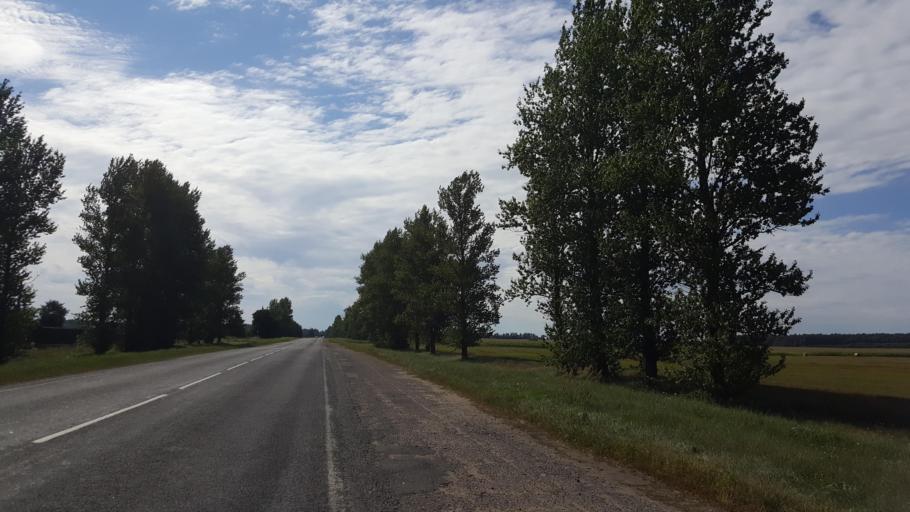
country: BY
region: Brest
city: Kamyanyets
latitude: 52.3566
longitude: 23.8949
